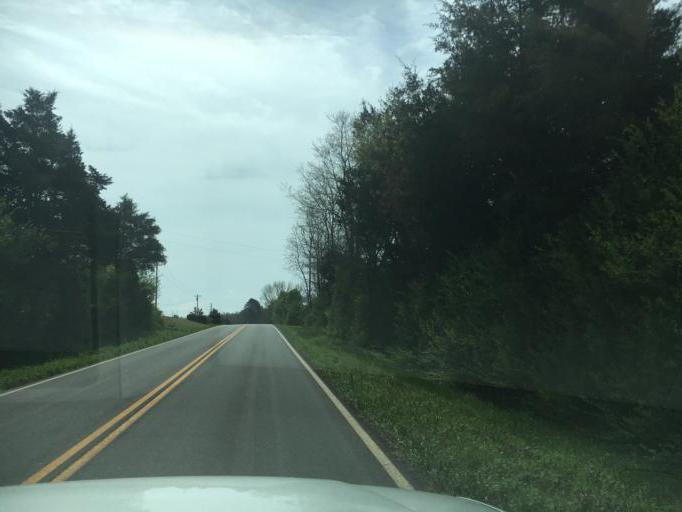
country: US
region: Georgia
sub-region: Franklin County
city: Lavonia
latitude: 34.3895
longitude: -83.0610
